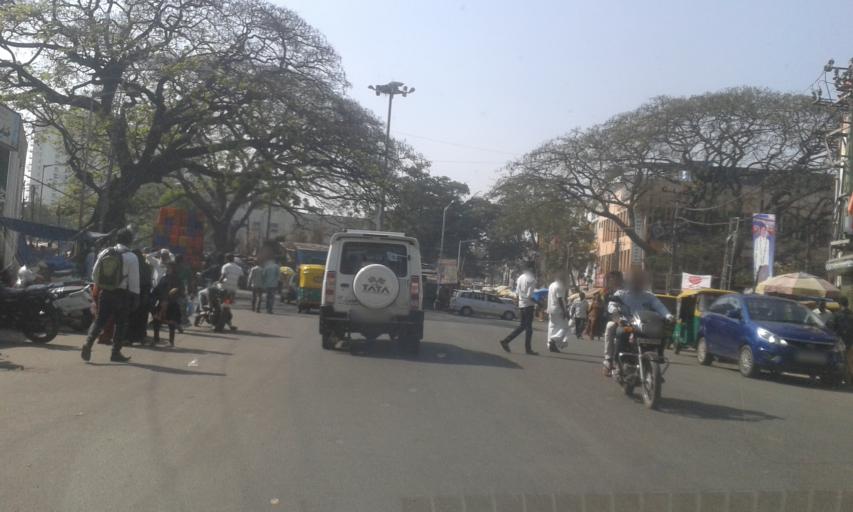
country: IN
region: Karnataka
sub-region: Bangalore Urban
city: Bangalore
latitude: 13.0197
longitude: 77.5560
